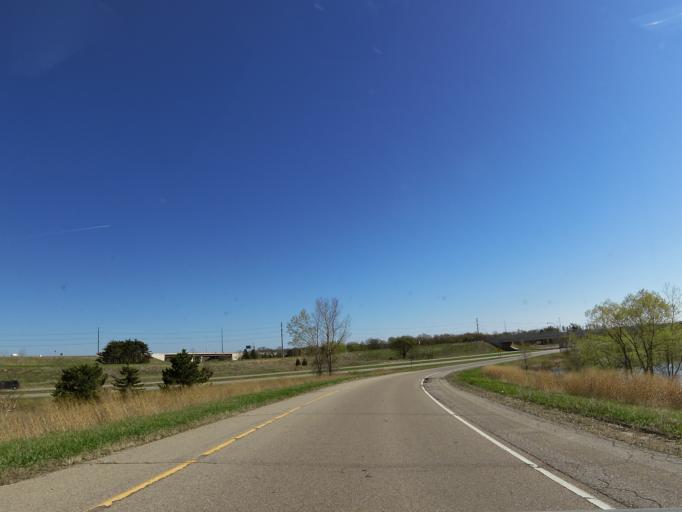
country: US
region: Minnesota
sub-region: Scott County
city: Prior Lake
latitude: 44.7827
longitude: -93.4121
